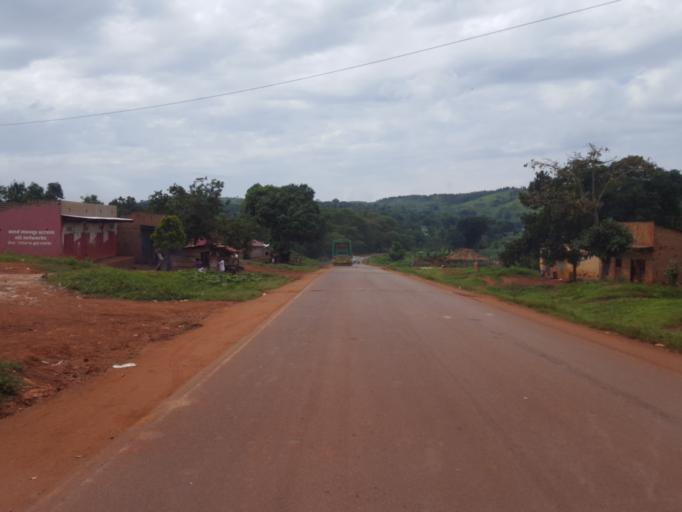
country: UG
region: Central Region
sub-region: Mityana District
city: Mityana
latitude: 0.6323
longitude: 32.1129
